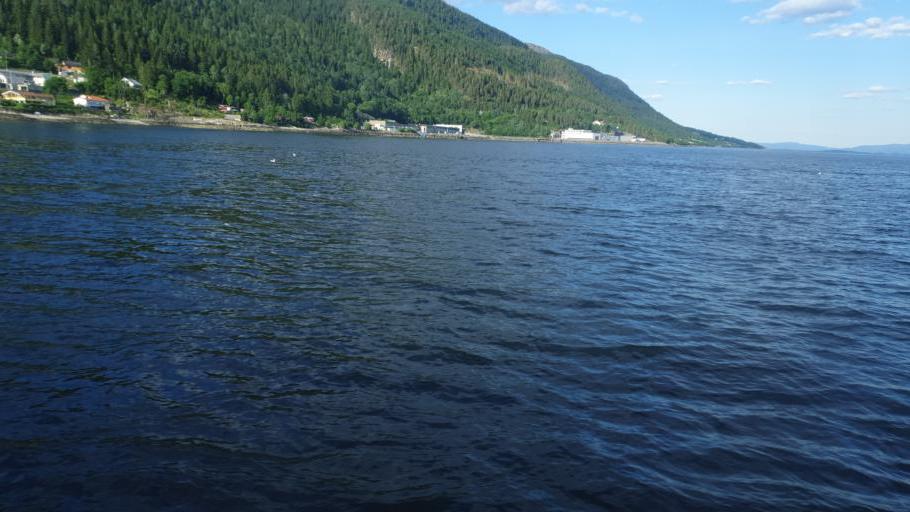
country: NO
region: Sor-Trondelag
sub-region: Trondheim
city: Trondheim
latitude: 63.5526
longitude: 10.2262
